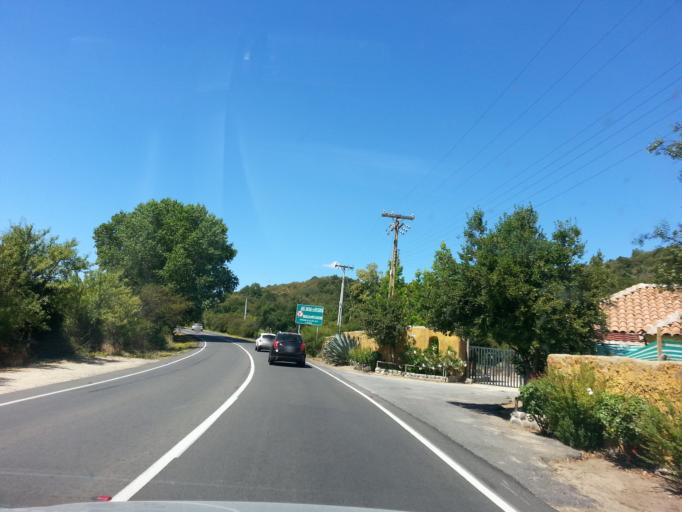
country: CL
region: Valparaiso
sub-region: Provincia de Marga Marga
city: Villa Alemana
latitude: -33.2009
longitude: -71.3786
